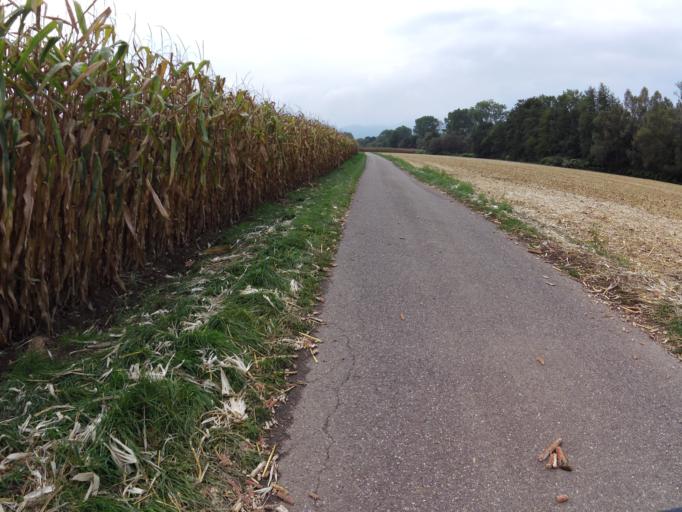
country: FR
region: Alsace
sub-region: Departement du Haut-Rhin
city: Guemar
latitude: 48.1859
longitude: 7.4186
